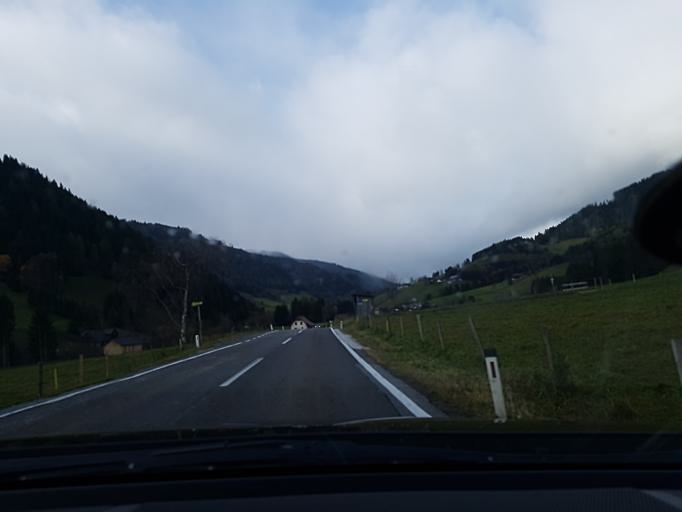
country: AT
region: Styria
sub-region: Politischer Bezirk Murtal
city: Sankt Johann am Tauern
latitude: 47.3127
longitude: 14.4832
